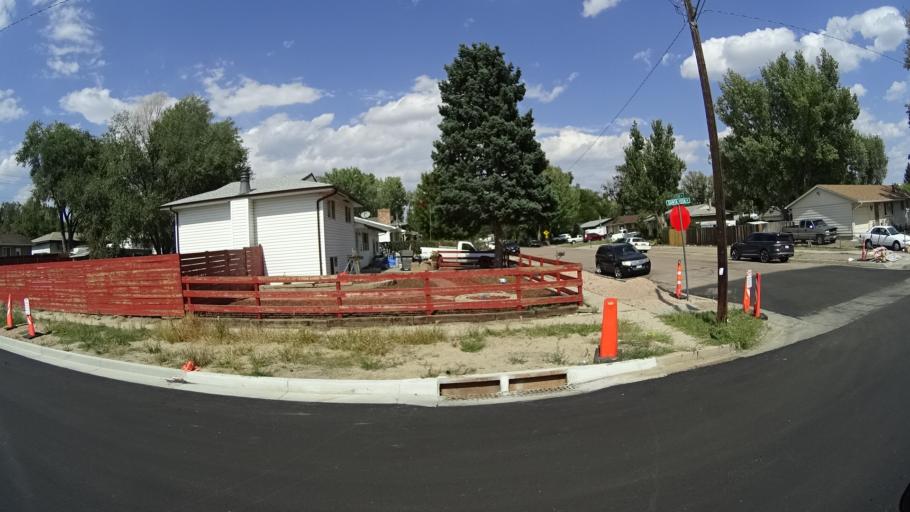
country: US
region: Colorado
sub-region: El Paso County
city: Colorado Springs
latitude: 38.8422
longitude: -104.7679
